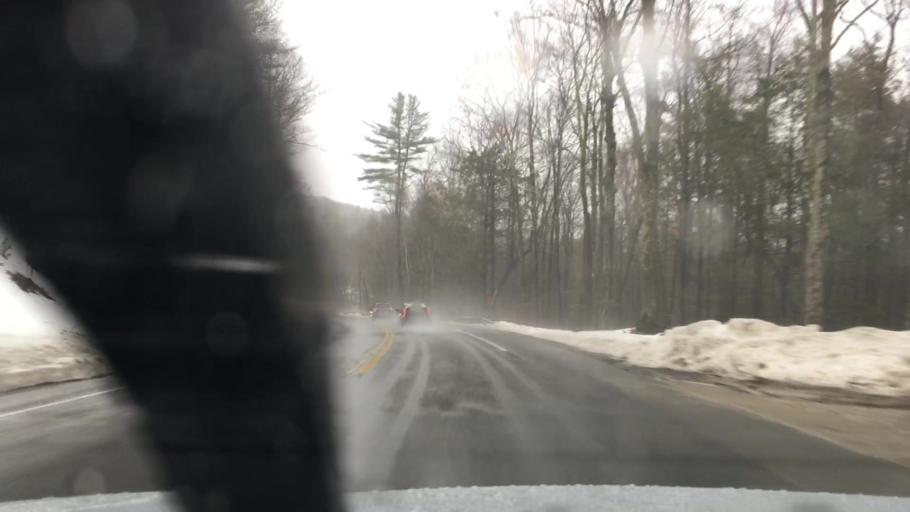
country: US
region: Massachusetts
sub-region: Franklin County
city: Shutesbury
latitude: 42.4736
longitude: -72.3508
